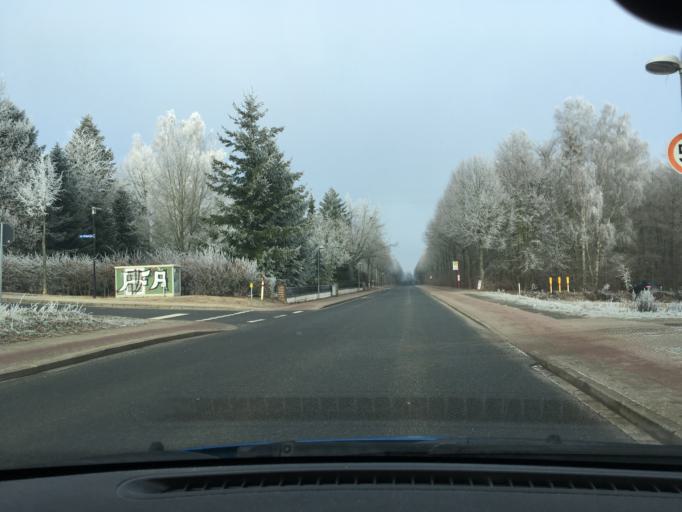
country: DE
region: Lower Saxony
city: Bardowick
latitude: 53.2658
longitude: 10.3899
